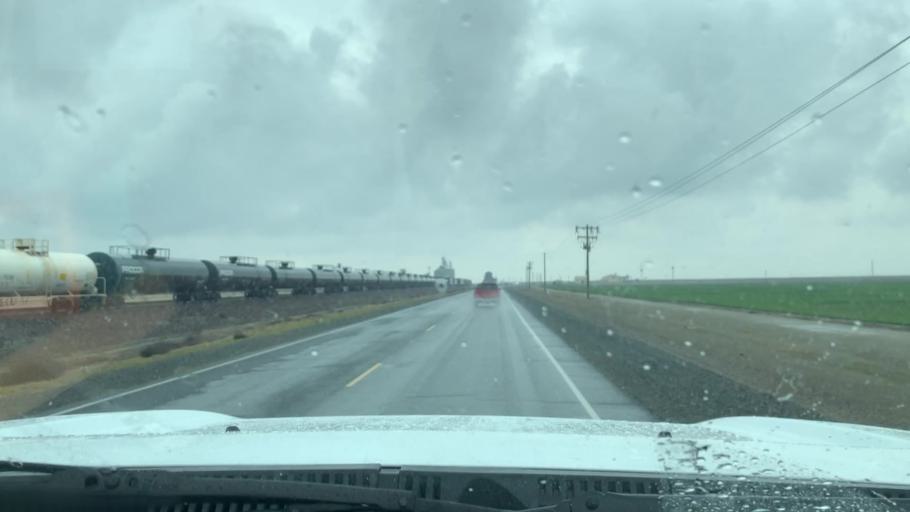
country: US
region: California
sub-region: Tulare County
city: Alpaugh
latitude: 35.9816
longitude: -119.4711
